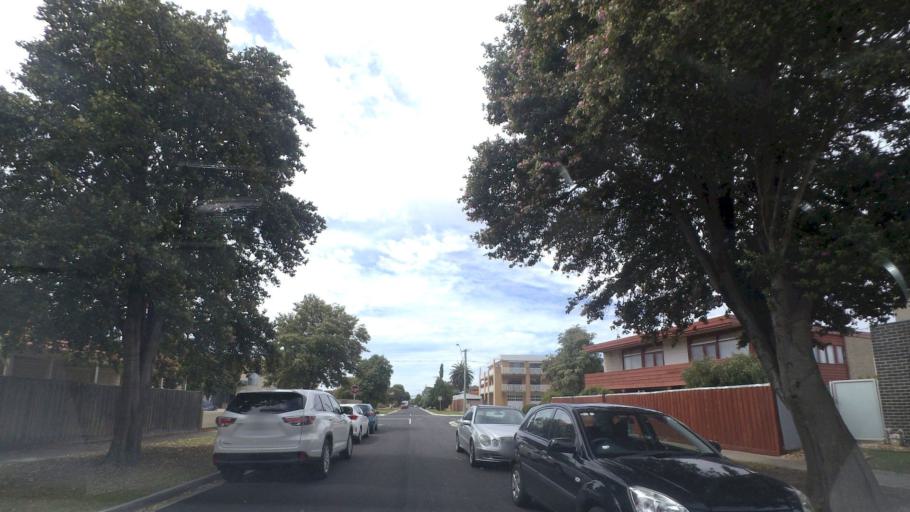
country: AU
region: Victoria
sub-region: Hobsons Bay
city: Altona
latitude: -37.8708
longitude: 144.8368
